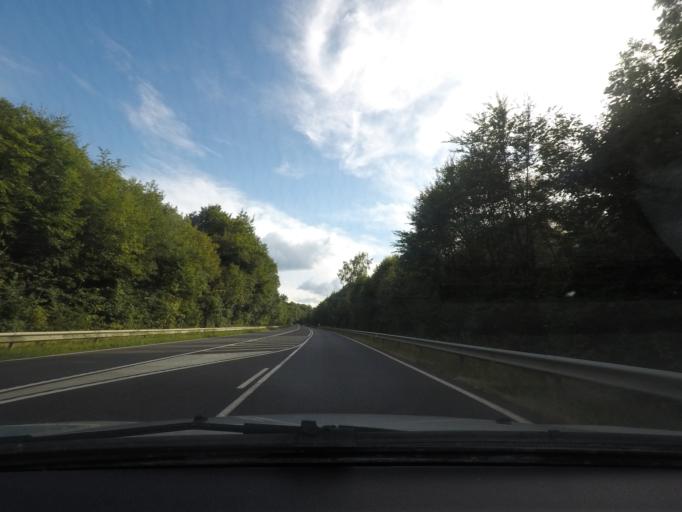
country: LU
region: Grevenmacher
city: Gonderange
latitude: 49.6697
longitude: 6.2052
